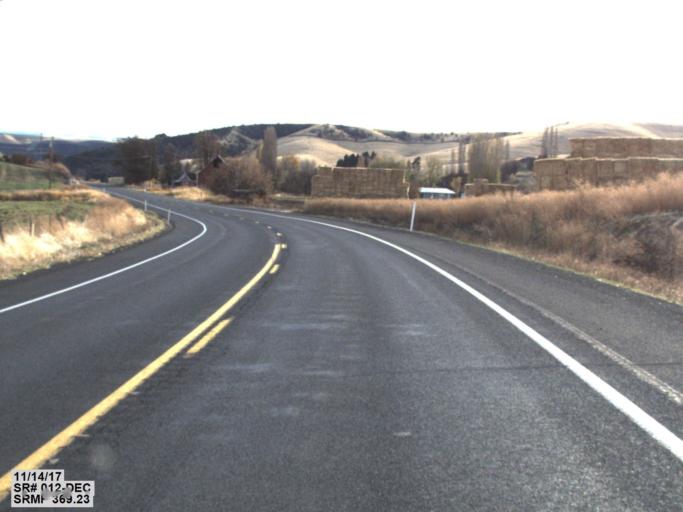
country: US
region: Washington
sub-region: Columbia County
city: Dayton
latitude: 46.3459
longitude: -117.9788
